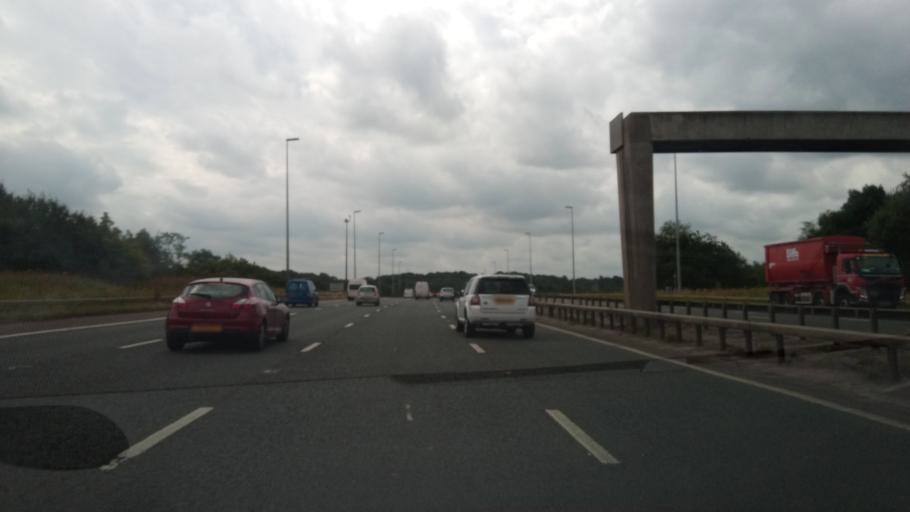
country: GB
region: England
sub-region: Lancashire
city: Goosnargh
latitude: 53.7676
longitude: -2.6364
